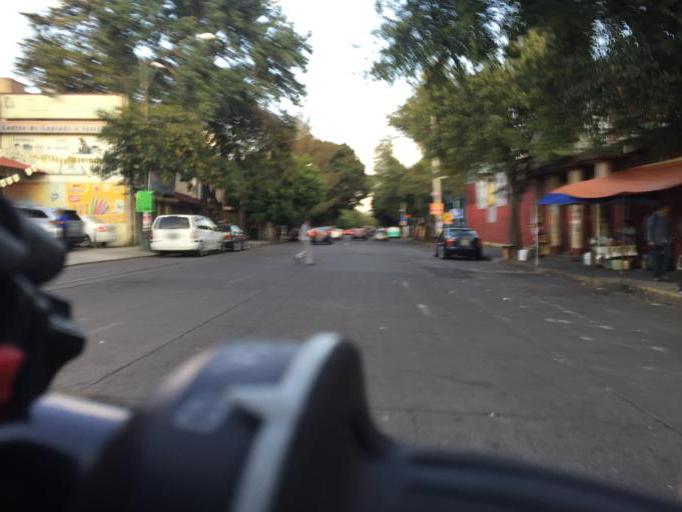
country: MX
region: Mexico City
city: Coyoacan
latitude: 19.3532
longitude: -99.1616
